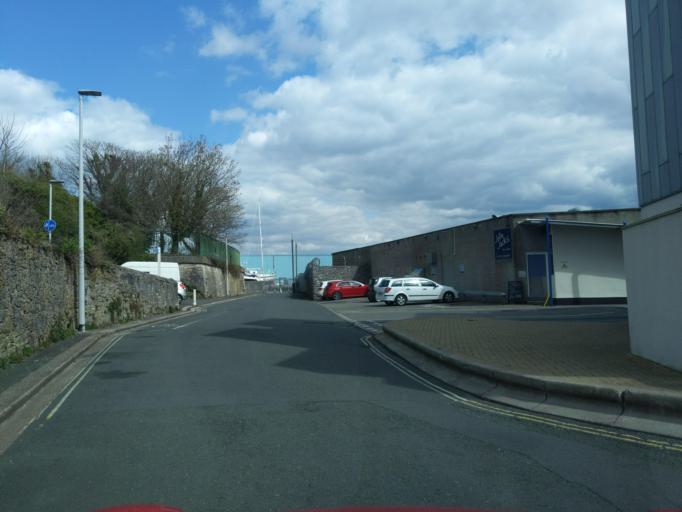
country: GB
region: England
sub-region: Cornwall
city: Millbrook
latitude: 50.3649
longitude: -4.1680
